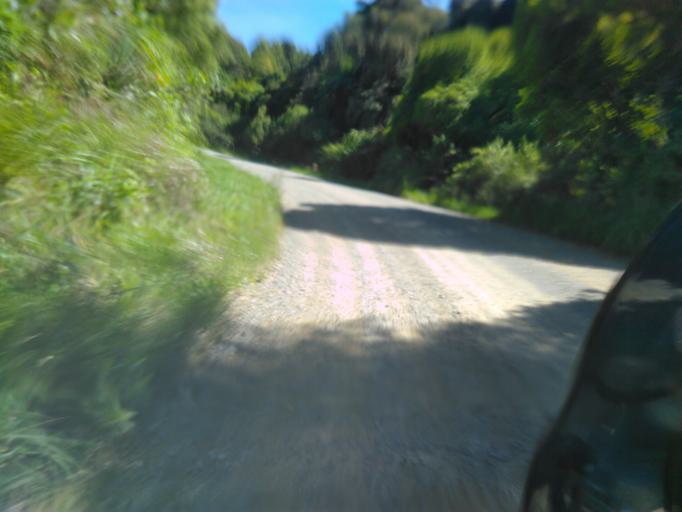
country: NZ
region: Hawke's Bay
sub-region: Wairoa District
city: Wairoa
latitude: -38.7946
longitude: 177.1251
